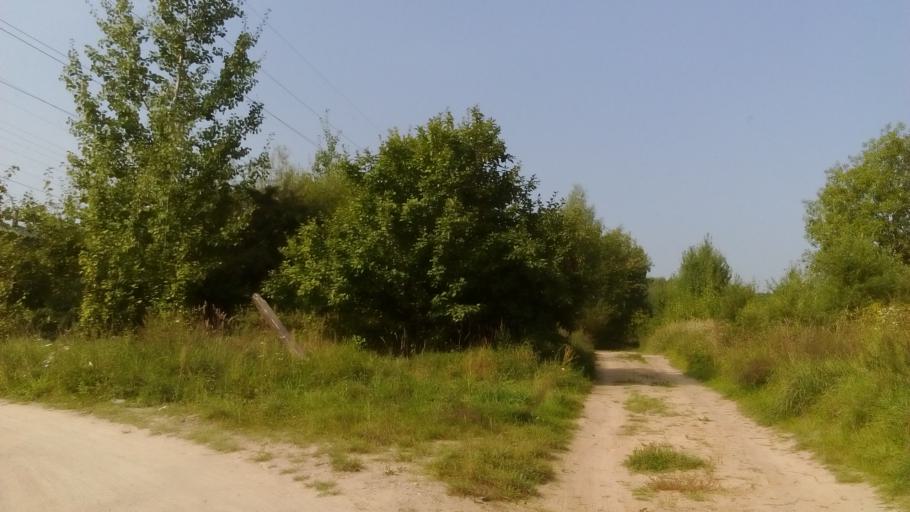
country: LT
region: Alytaus apskritis
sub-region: Alytus
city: Alytus
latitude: 54.3889
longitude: 24.0177
